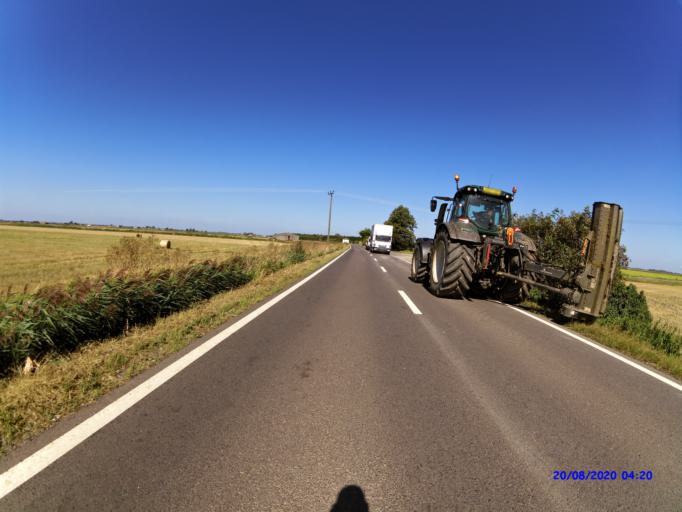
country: GB
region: England
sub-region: Cambridgeshire
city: Ramsey
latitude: 52.4940
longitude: -0.1207
